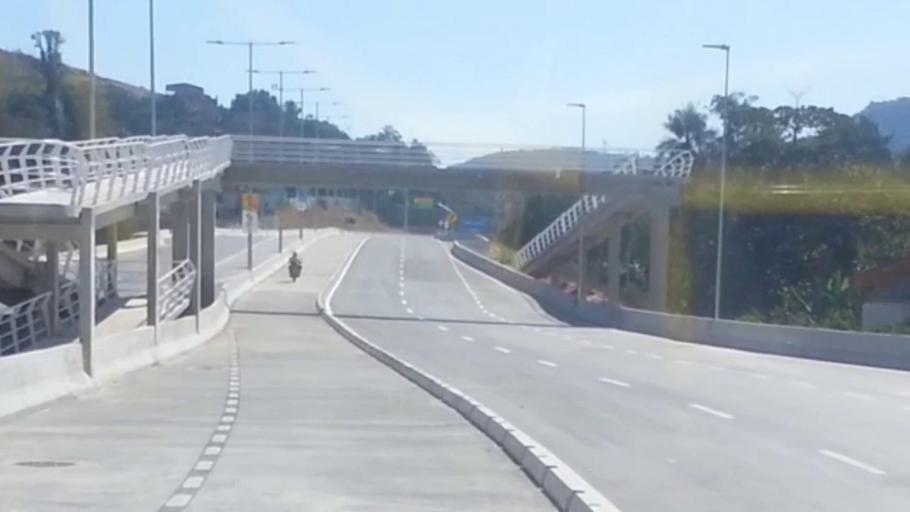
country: BR
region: Rio de Janeiro
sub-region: Nilopolis
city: Nilopolis
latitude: -22.9275
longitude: -43.3960
